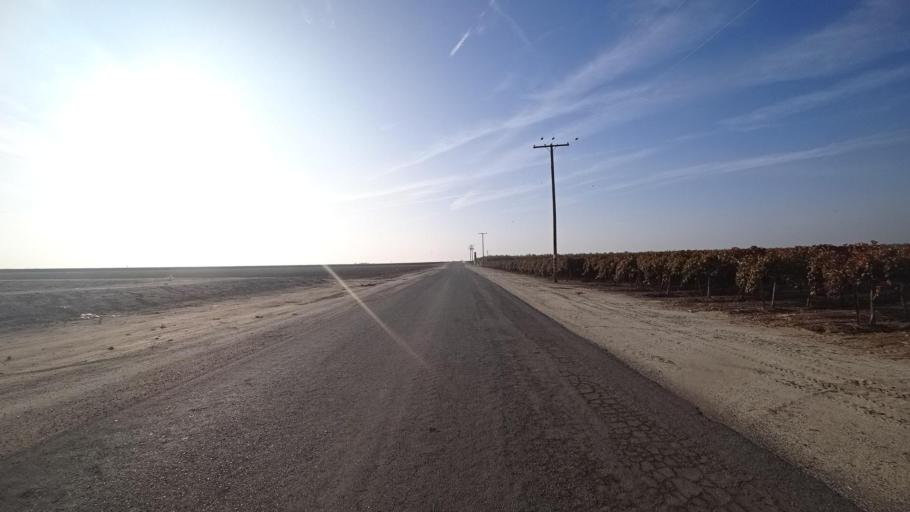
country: US
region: California
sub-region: Kern County
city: McFarland
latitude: 35.7164
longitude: -119.1872
